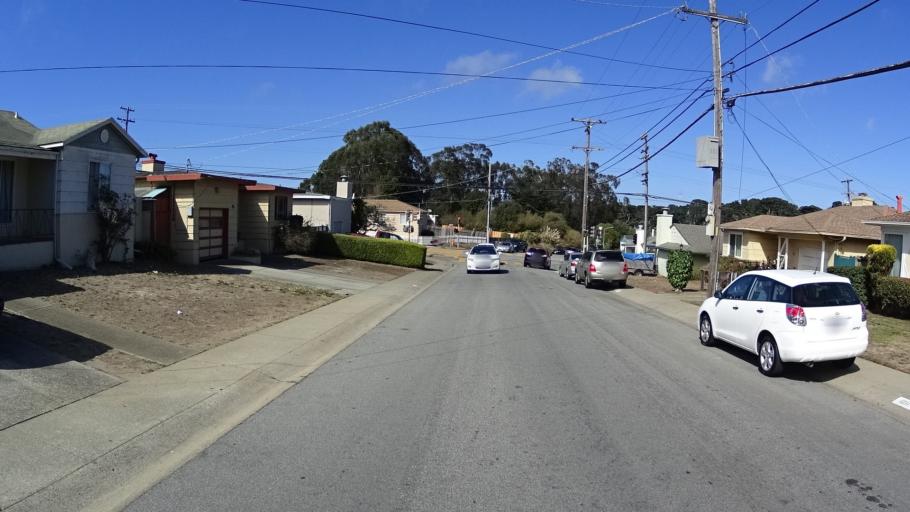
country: US
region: California
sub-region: San Mateo County
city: Broadmoor
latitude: 37.6927
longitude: -122.4803
